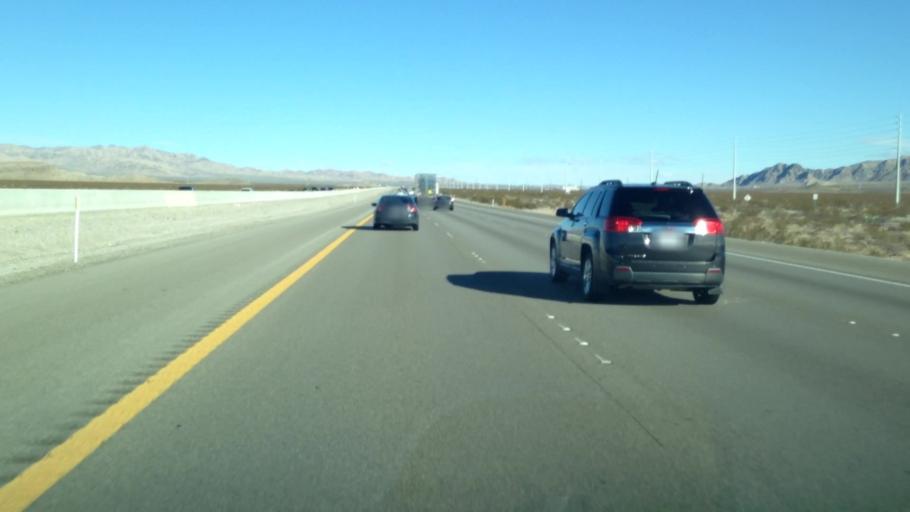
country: US
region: Nevada
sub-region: Clark County
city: Sandy Valley
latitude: 35.7148
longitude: -115.3652
